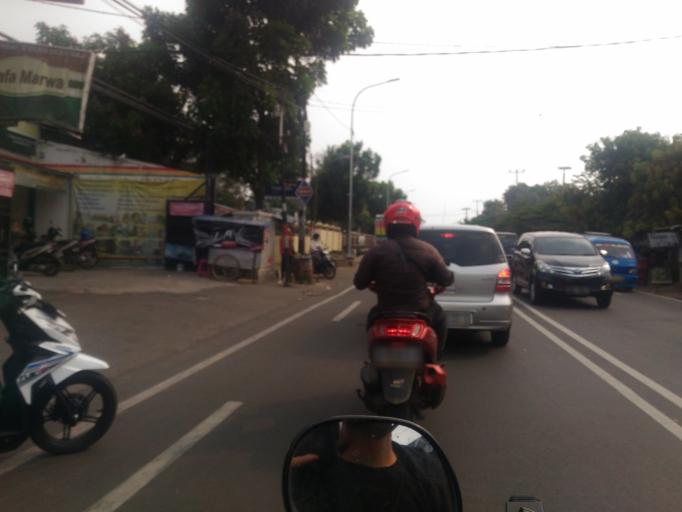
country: ID
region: West Java
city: Bogor
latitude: -6.5524
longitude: 106.8209
